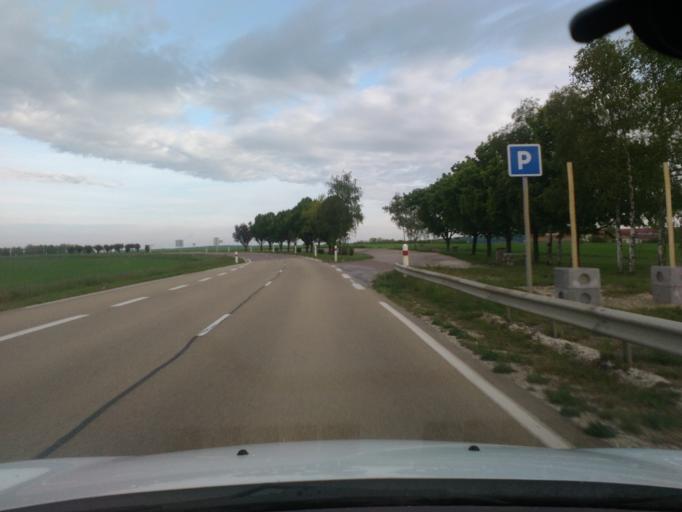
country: FR
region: Champagne-Ardenne
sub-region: Departement de la Haute-Marne
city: Lavilleneuve-au-Roi
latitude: 48.2282
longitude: 4.8720
